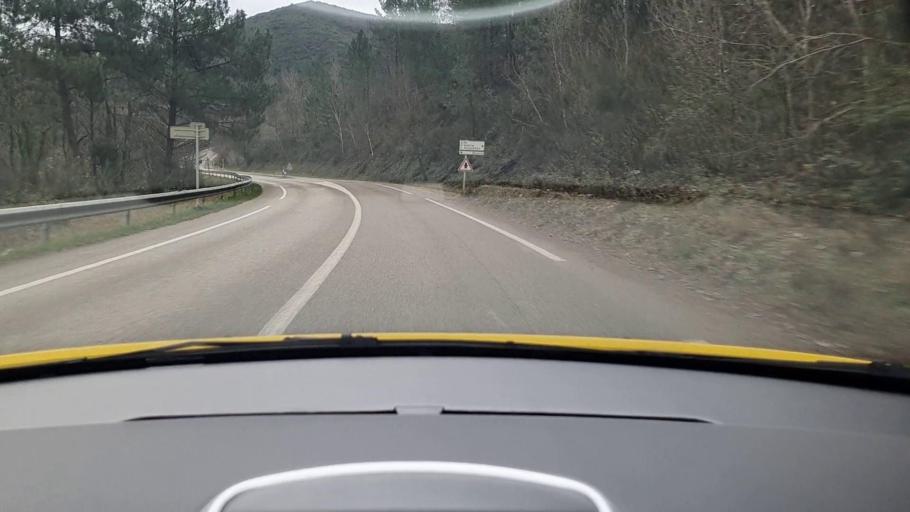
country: FR
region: Languedoc-Roussillon
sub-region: Departement du Gard
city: Laval-Pradel
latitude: 44.2246
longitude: 4.0782
